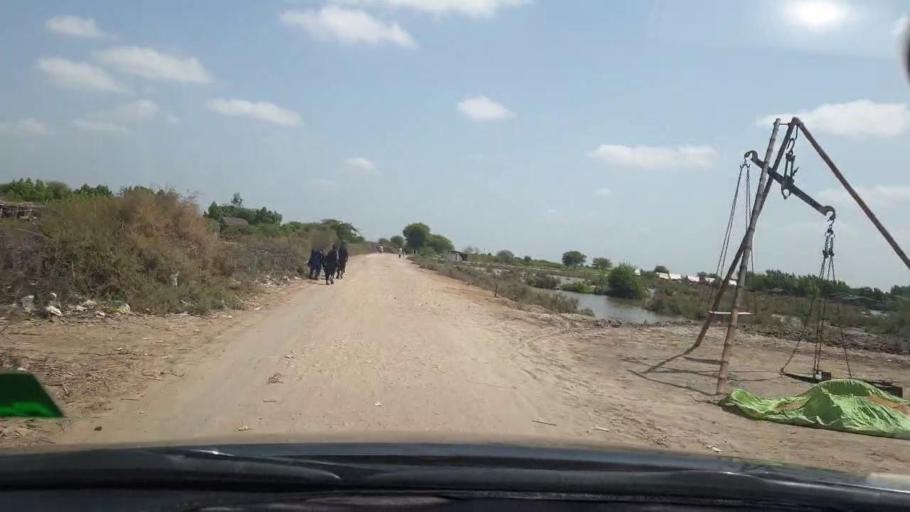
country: PK
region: Sindh
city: Tando Bago
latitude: 24.8817
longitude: 69.0777
